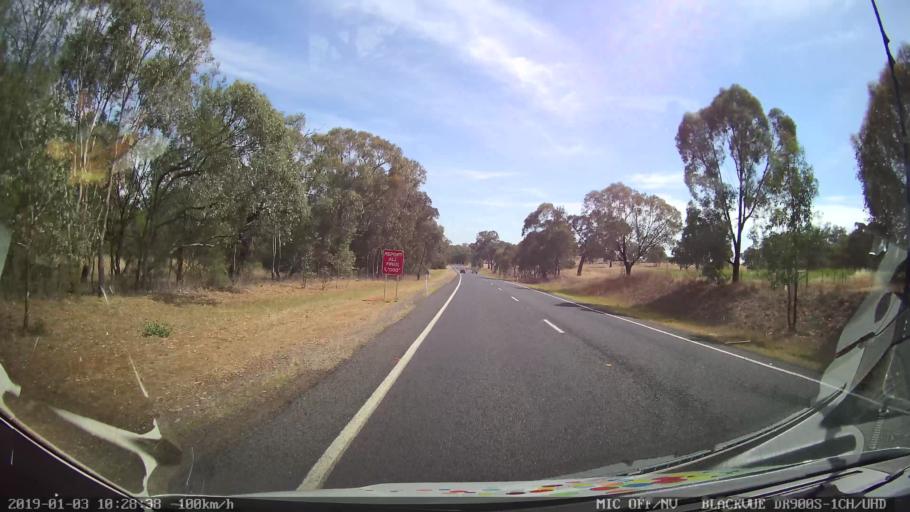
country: AU
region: New South Wales
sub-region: Young
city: Young
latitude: -34.3853
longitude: 148.2593
